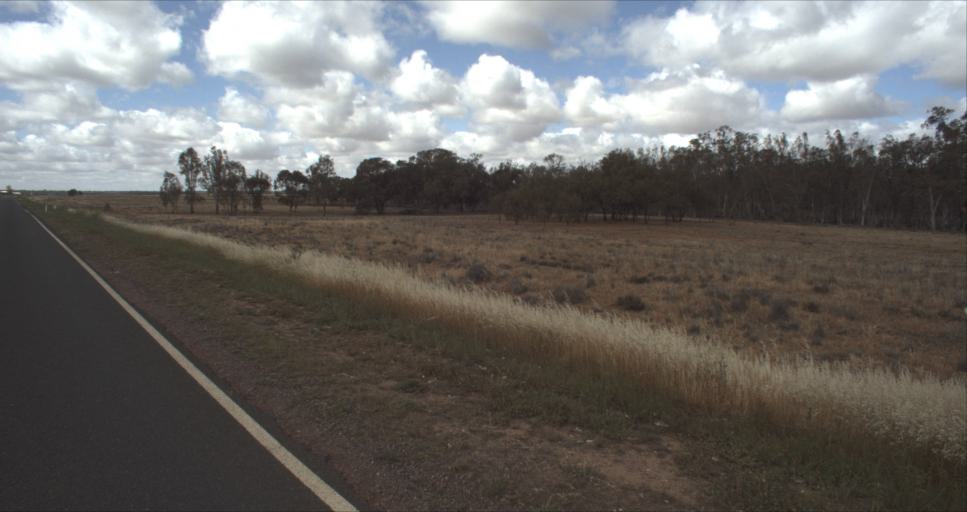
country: AU
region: New South Wales
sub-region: Murrumbidgee Shire
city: Darlington Point
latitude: -34.5779
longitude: 146.1069
